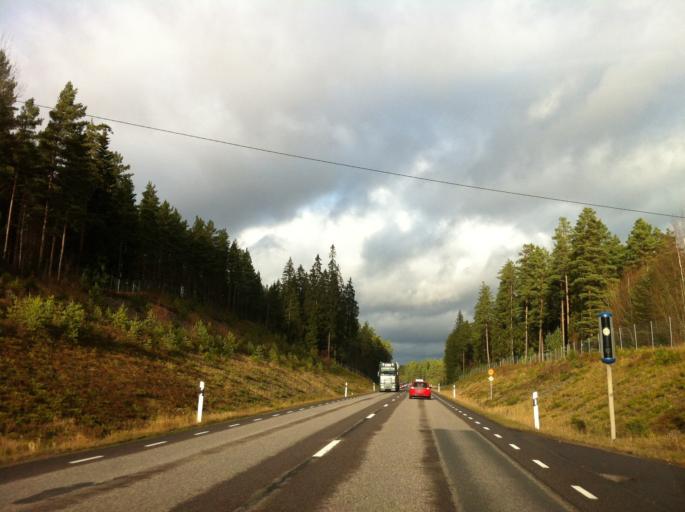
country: SE
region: Kalmar
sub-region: Vimmerby Kommun
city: Vimmerby
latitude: 57.6057
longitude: 15.8443
